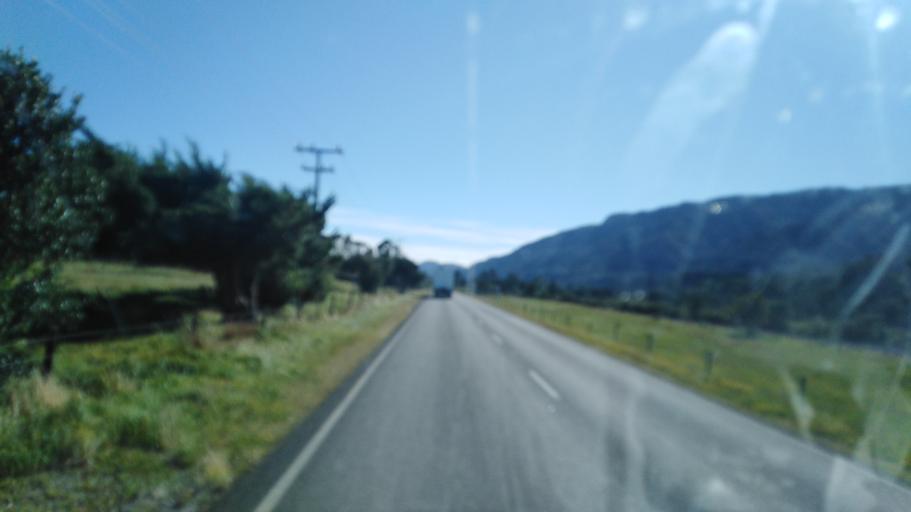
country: NZ
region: West Coast
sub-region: Buller District
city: Westport
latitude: -41.6740
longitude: 171.8009
